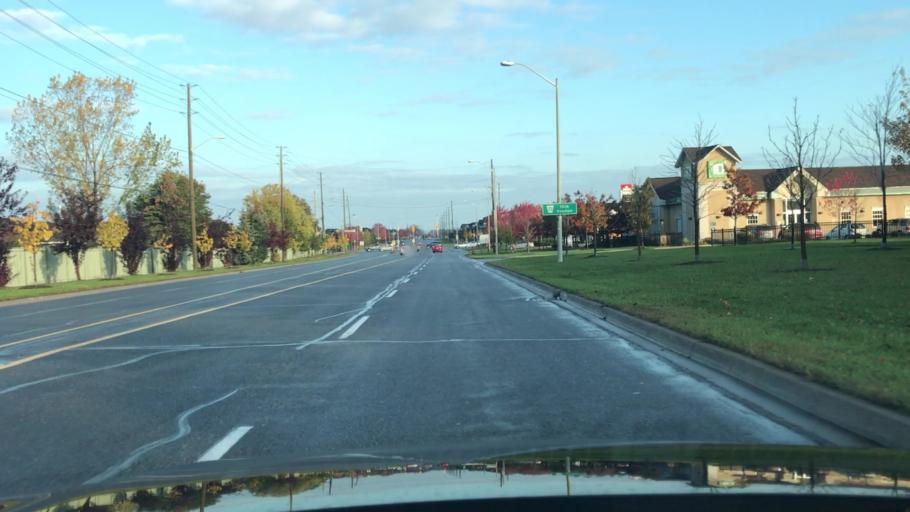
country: CA
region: Ontario
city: Markham
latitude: 43.8957
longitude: -79.2390
